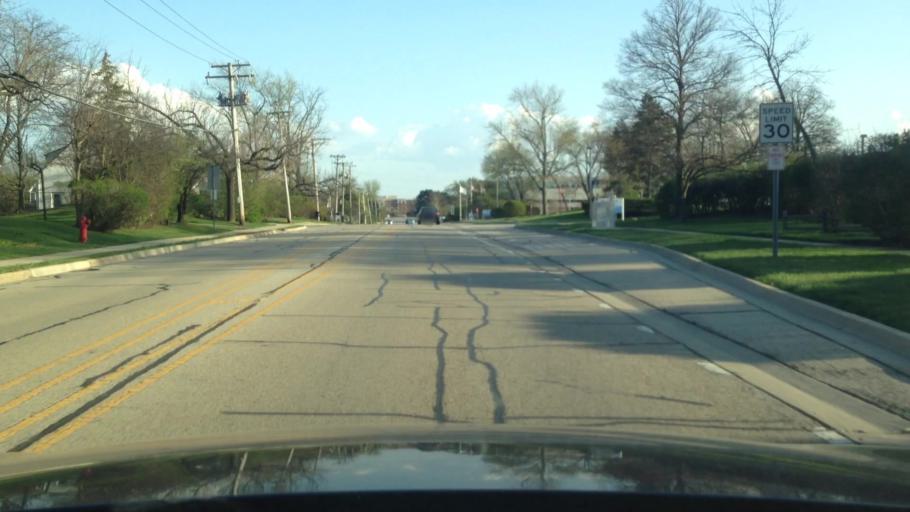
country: US
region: Illinois
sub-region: Lake County
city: Deerfield
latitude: 42.1591
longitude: -87.8674
